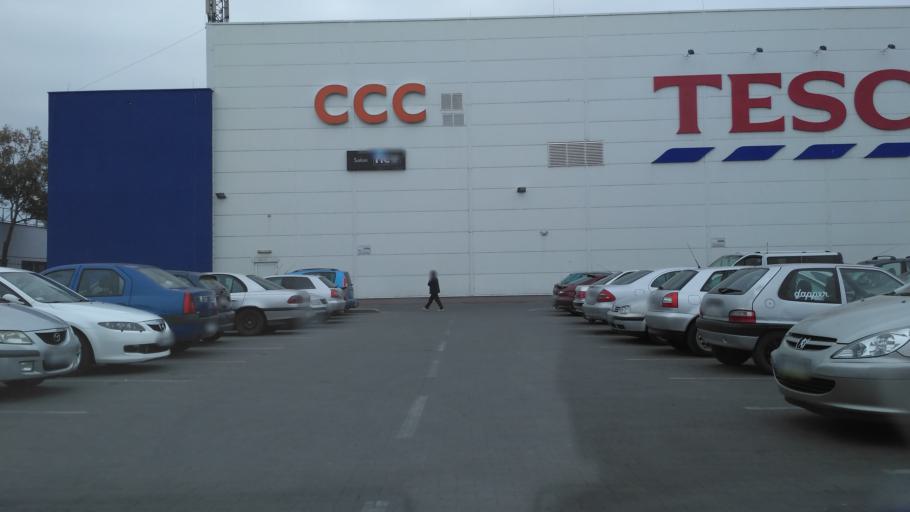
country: PL
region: Lublin Voivodeship
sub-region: Chelm
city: Chelm
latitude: 51.1267
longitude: 23.4681
